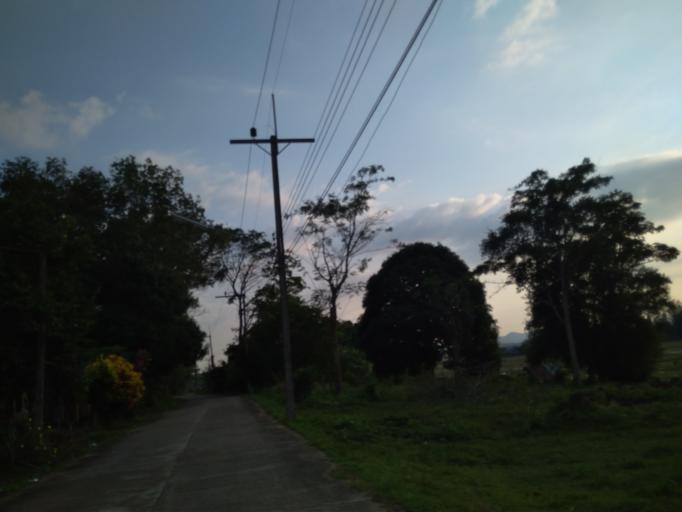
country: TH
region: Phangnga
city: Ko Yao
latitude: 8.1382
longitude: 98.5983
